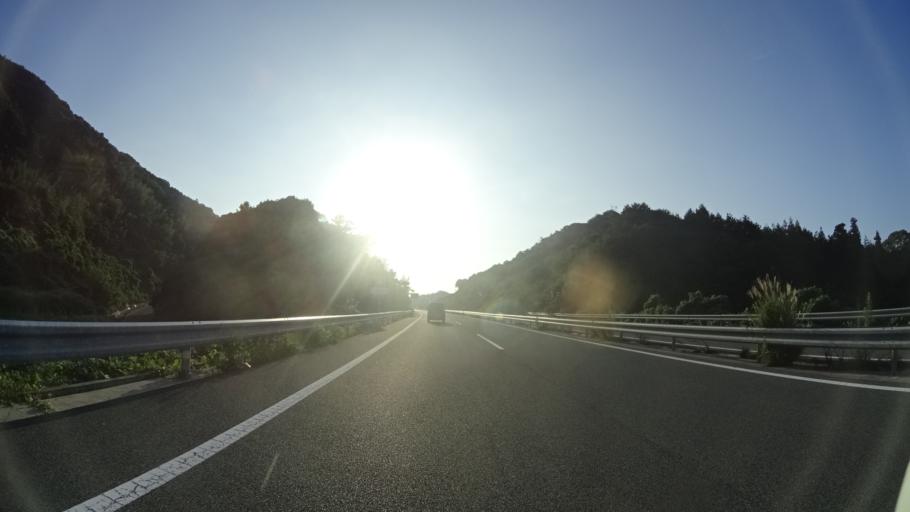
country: JP
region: Yamaguchi
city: Hagi
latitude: 34.3891
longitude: 131.3300
